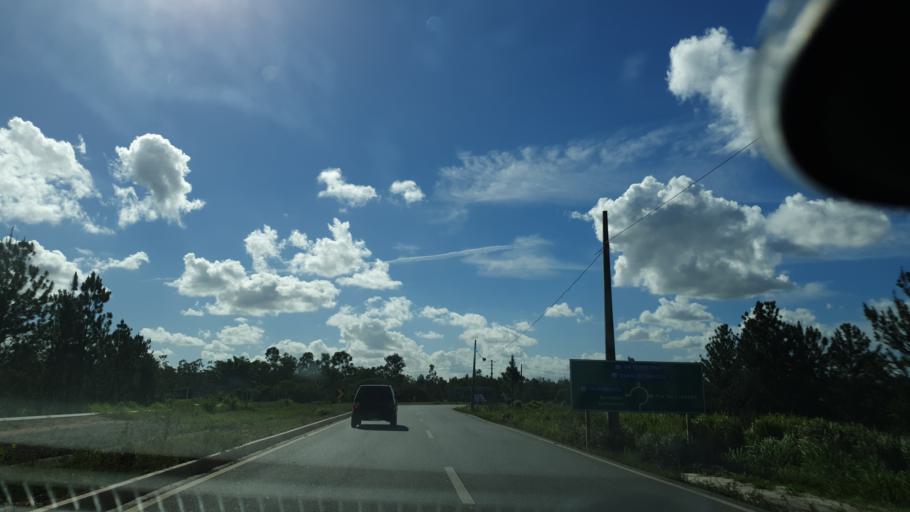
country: BR
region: Bahia
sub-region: Camacari
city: Camacari
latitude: -12.6825
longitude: -38.3003
